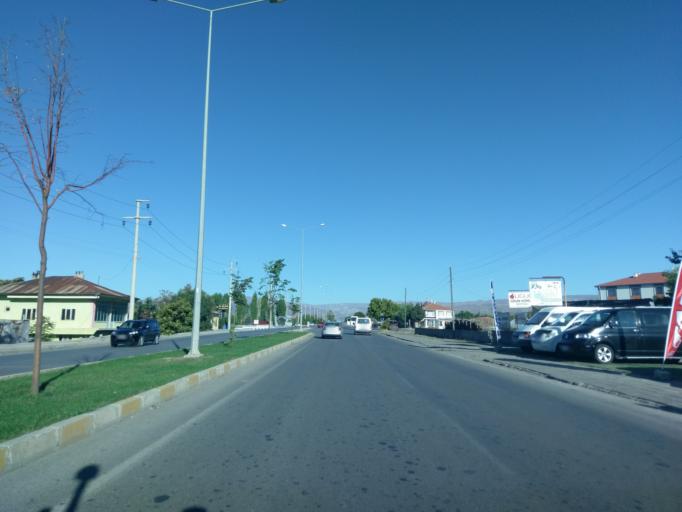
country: TR
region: Erzincan
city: Erzincan
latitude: 39.7520
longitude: 39.4561
